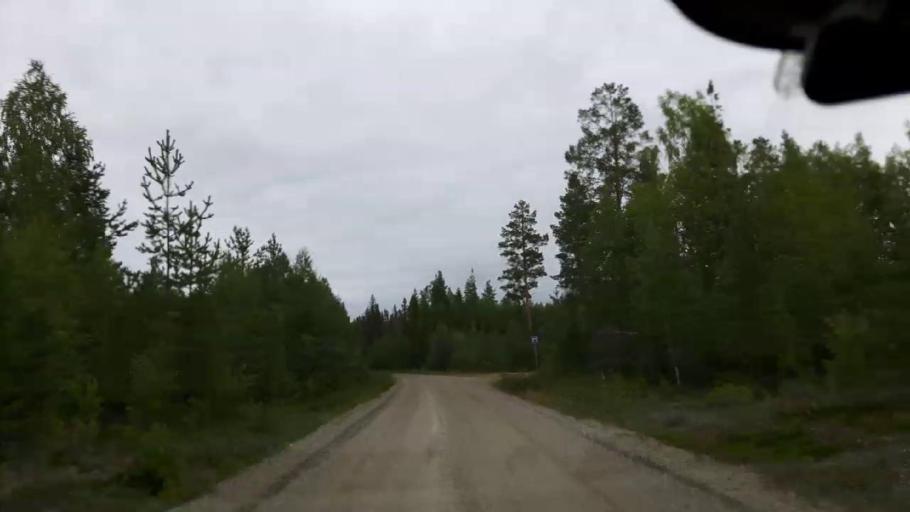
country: SE
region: Vaesternorrland
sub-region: Ange Kommun
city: Ange
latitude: 62.8116
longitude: 15.7252
